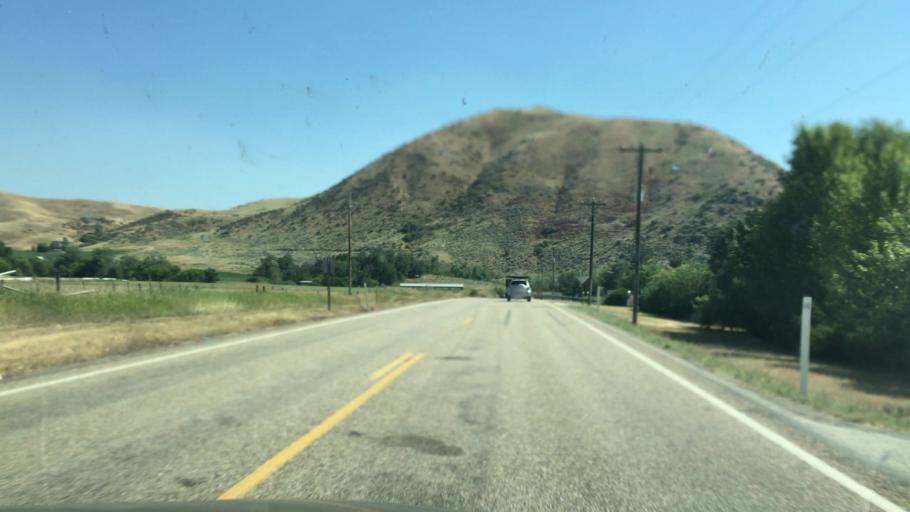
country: US
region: Idaho
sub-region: Ada County
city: Eagle
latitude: 43.9679
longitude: -116.1885
